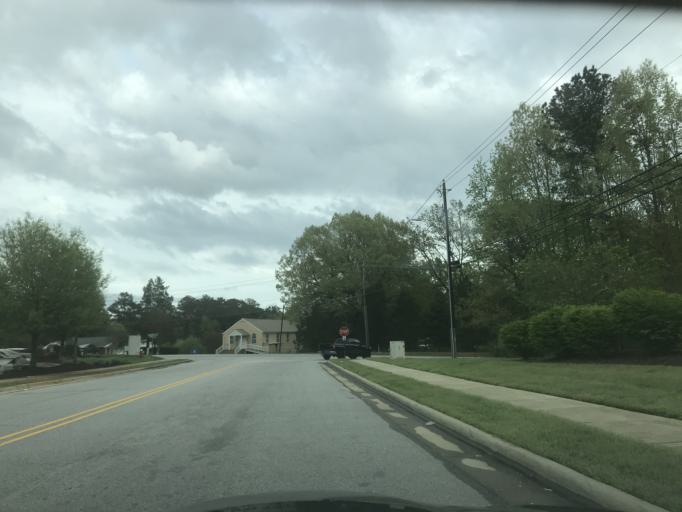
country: US
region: North Carolina
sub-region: Wake County
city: West Raleigh
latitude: 35.7472
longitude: -78.6758
